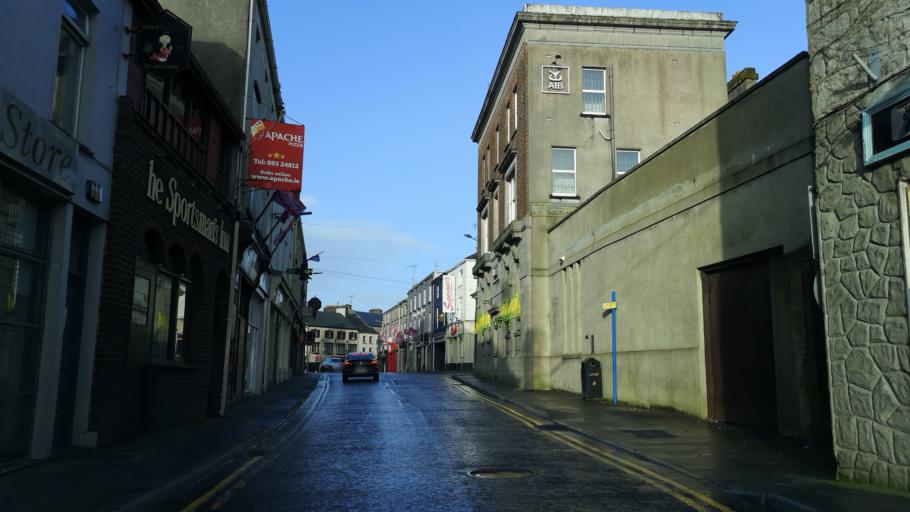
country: IE
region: Connaught
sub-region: County Galway
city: Tuam
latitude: 53.5140
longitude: -8.8515
